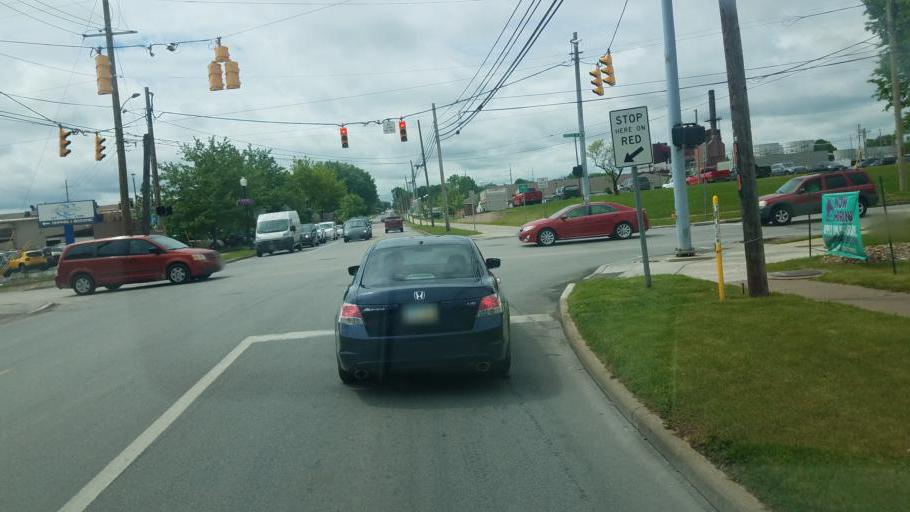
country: US
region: Ohio
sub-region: Wayne County
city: Orrville
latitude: 40.8537
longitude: -81.7639
